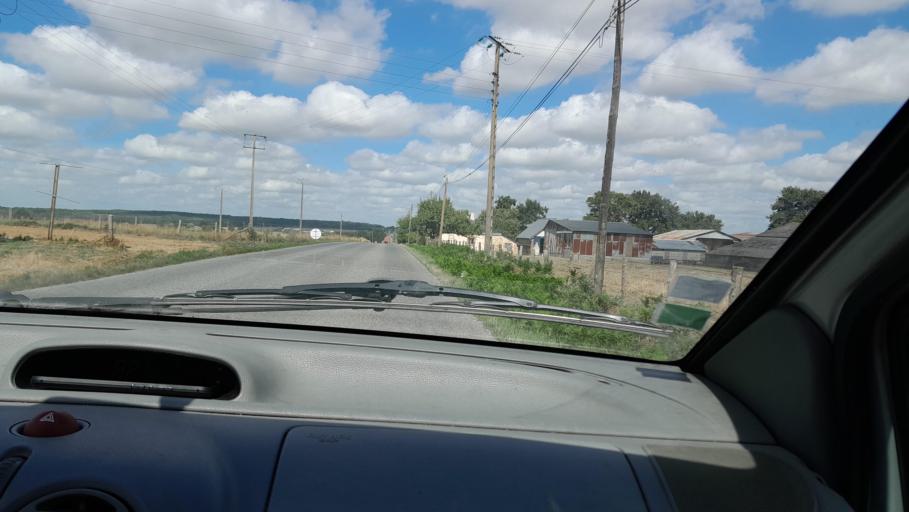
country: FR
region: Pays de la Loire
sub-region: Departement de la Mayenne
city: Craon
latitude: 47.8700
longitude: -0.9979
